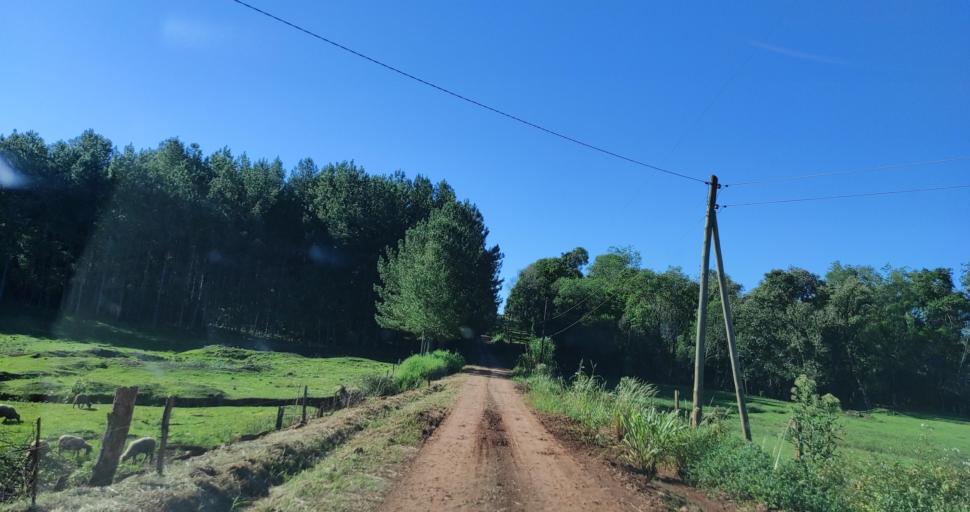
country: AR
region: Misiones
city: Capiovi
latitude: -26.9220
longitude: -55.0004
